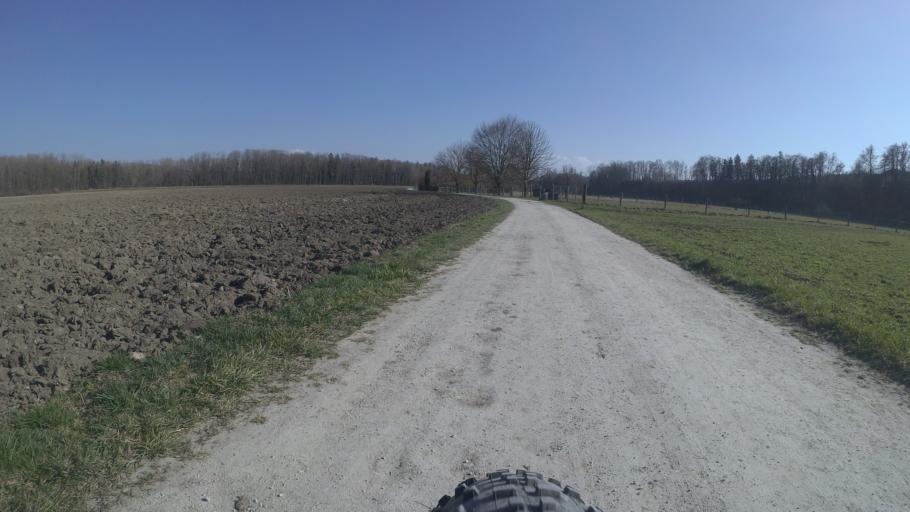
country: DE
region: Bavaria
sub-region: Upper Bavaria
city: Nussdorf
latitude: 47.9311
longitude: 12.6068
